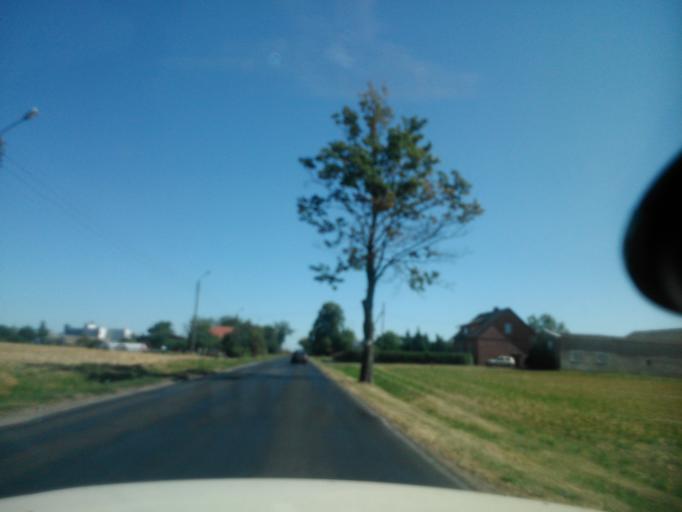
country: PL
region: Kujawsko-Pomorskie
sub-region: Powiat golubsko-dobrzynski
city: Golub-Dobrzyn
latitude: 53.1238
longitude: 19.0366
